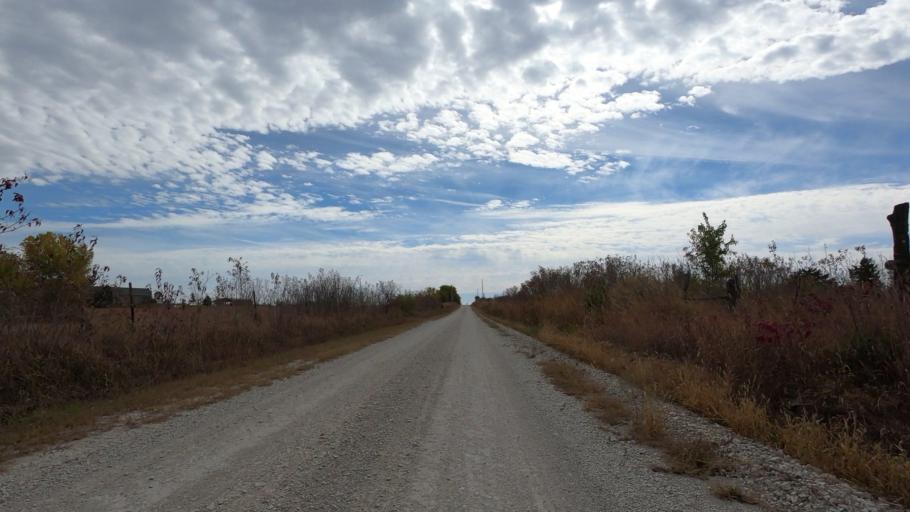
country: US
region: Kansas
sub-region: Pottawatomie County
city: Westmoreland
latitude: 39.3405
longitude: -96.4453
